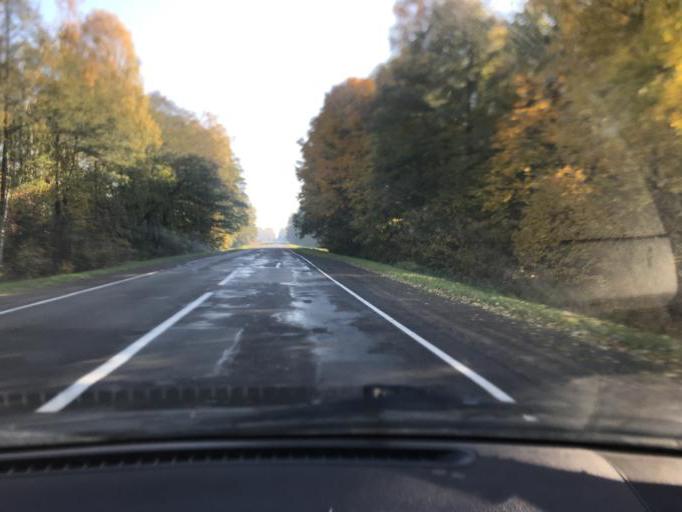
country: BY
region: Brest
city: Lyakhavichy
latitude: 52.9490
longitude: 26.1309
